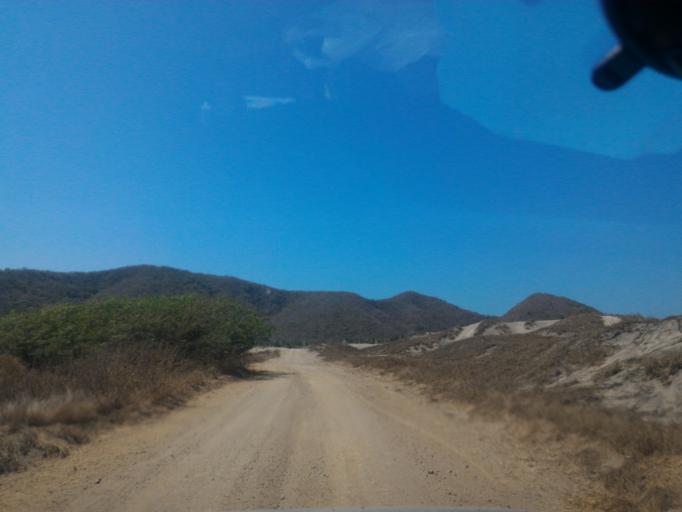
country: MX
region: Michoacan
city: Coahuayana Viejo
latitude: 18.5933
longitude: -103.6945
